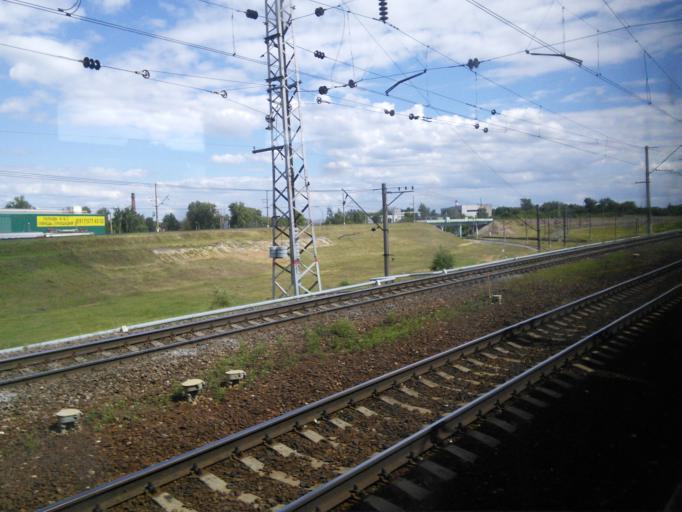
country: RU
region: Moscow
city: Nekrasovka
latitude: 55.6726
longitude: 37.9159
